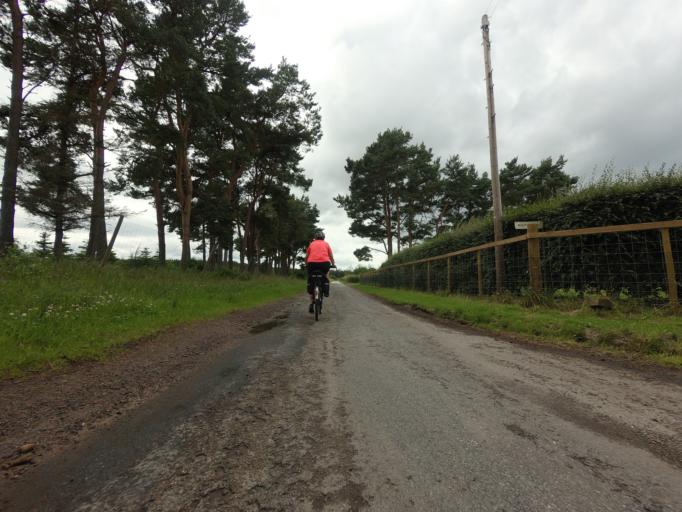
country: GB
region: Scotland
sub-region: Highland
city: Nairn
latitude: 57.6020
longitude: -3.7754
